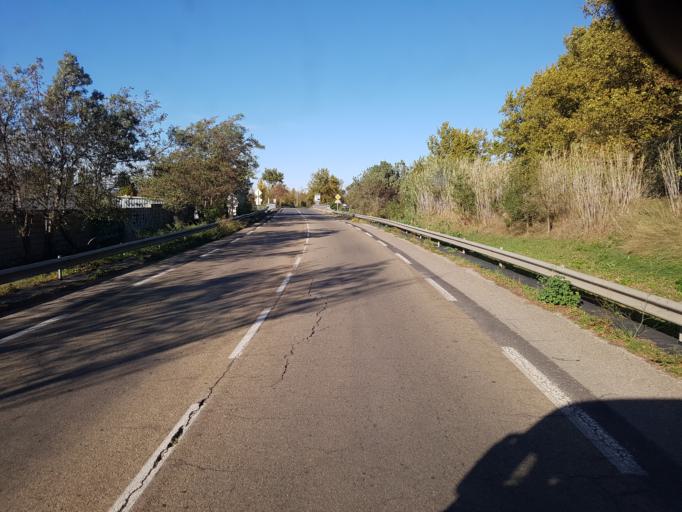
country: FR
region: Languedoc-Roussillon
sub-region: Departement de l'Aude
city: Coursan
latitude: 43.2386
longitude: 3.0592
